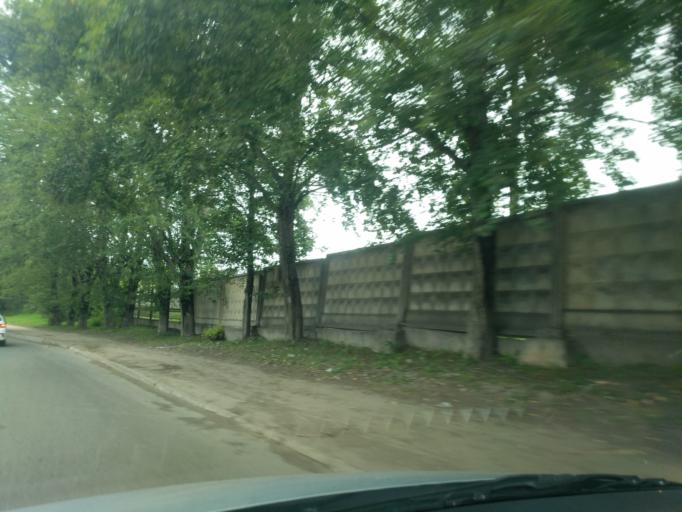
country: RU
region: Kirov
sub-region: Kirovo-Chepetskiy Rayon
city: Kirov
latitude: 58.6337
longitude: 49.6145
